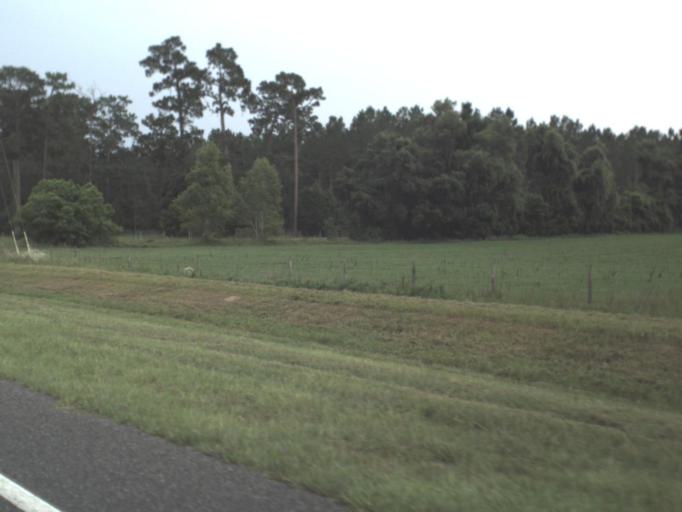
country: US
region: Florida
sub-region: Levy County
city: Chiefland
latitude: 29.4747
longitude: -82.8237
